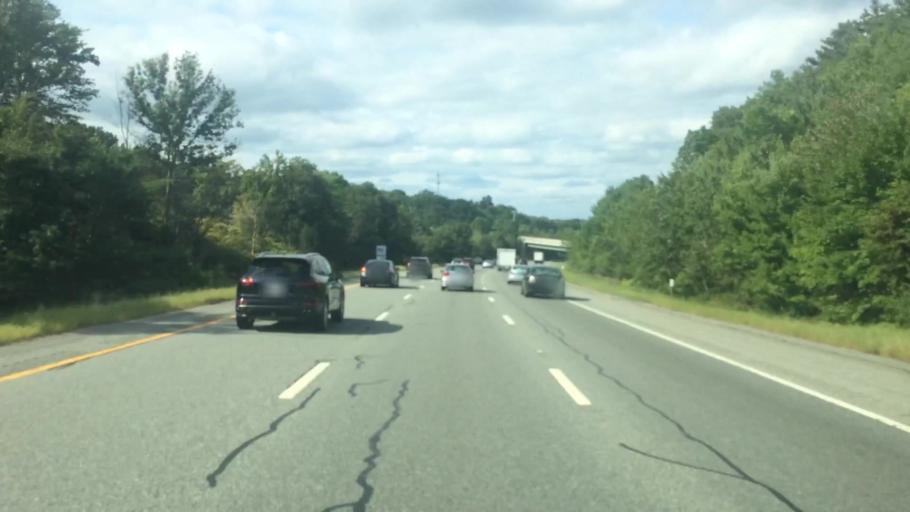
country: US
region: Rhode Island
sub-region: Providence County
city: Greenville
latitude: 41.8924
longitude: -71.5223
